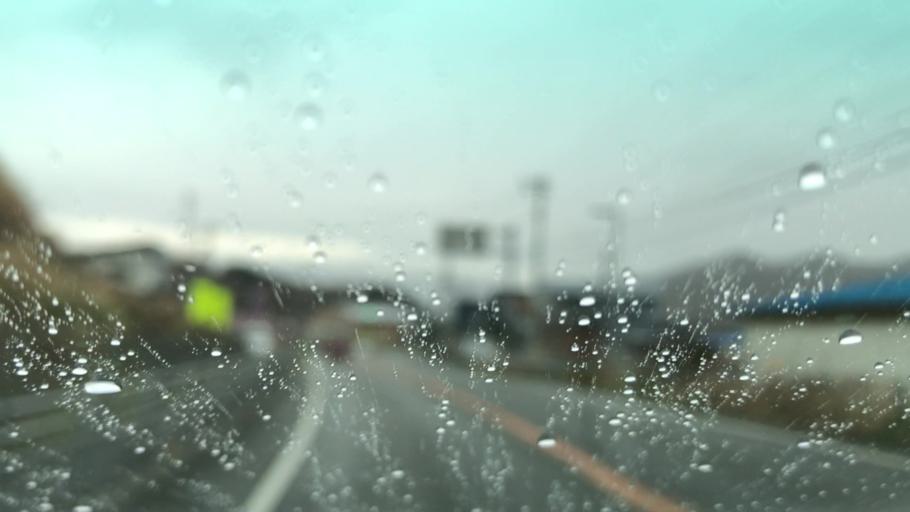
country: JP
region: Hokkaido
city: Shizunai-furukawacho
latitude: 42.2673
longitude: 142.4974
